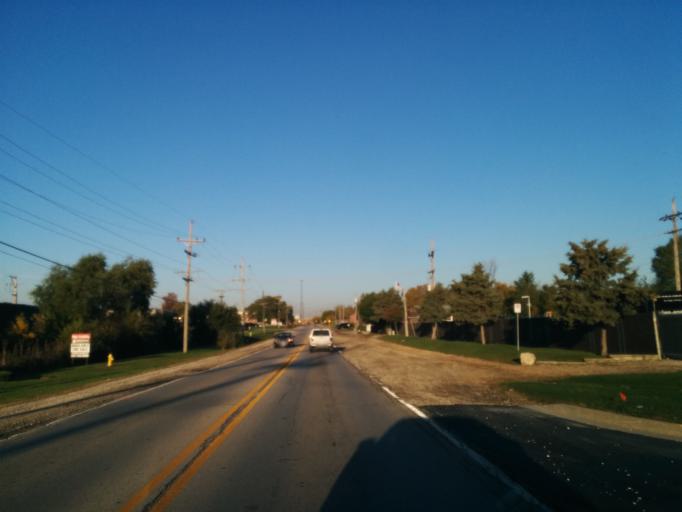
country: US
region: Illinois
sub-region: DuPage County
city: Carol Stream
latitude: 41.8980
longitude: -88.1092
